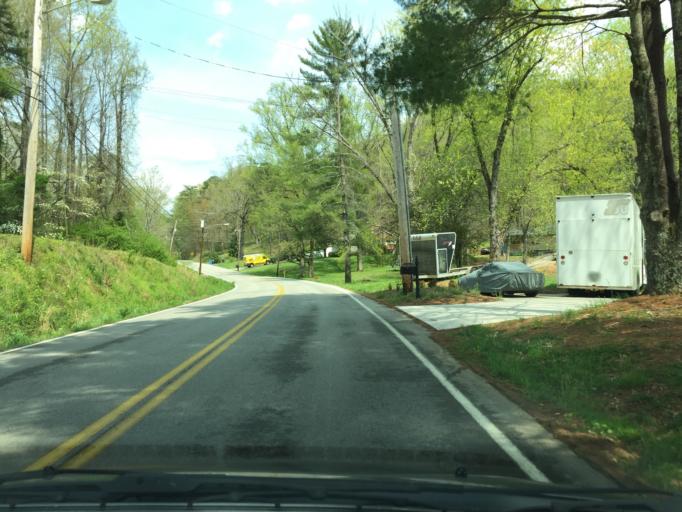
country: US
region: Tennessee
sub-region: Hamilton County
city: Walden
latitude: 35.1469
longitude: -85.2865
